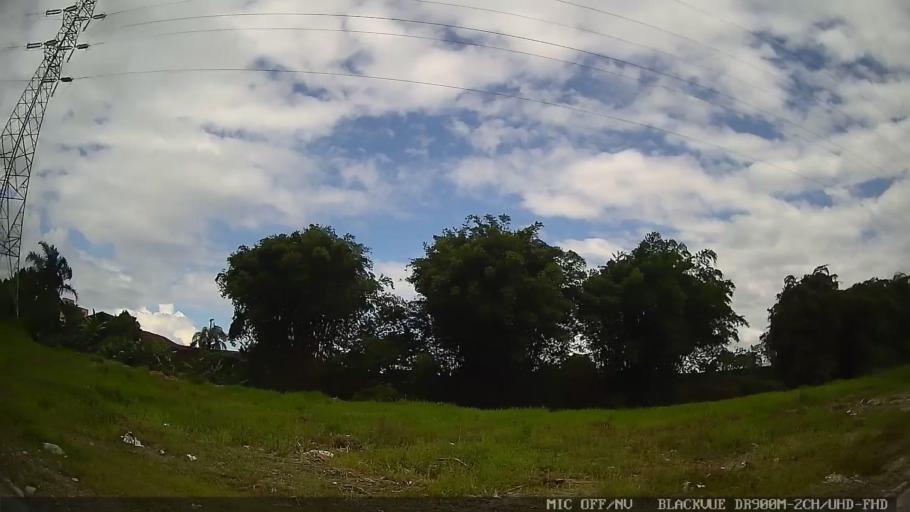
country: BR
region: Sao Paulo
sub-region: Caraguatatuba
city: Caraguatatuba
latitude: -23.6346
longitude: -45.4360
